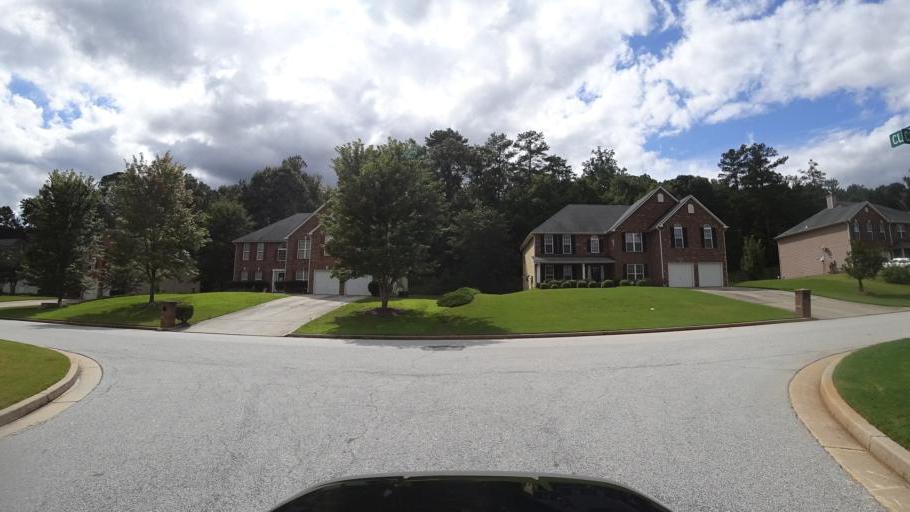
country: US
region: Georgia
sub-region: DeKalb County
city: Panthersville
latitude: 33.6503
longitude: -84.2217
